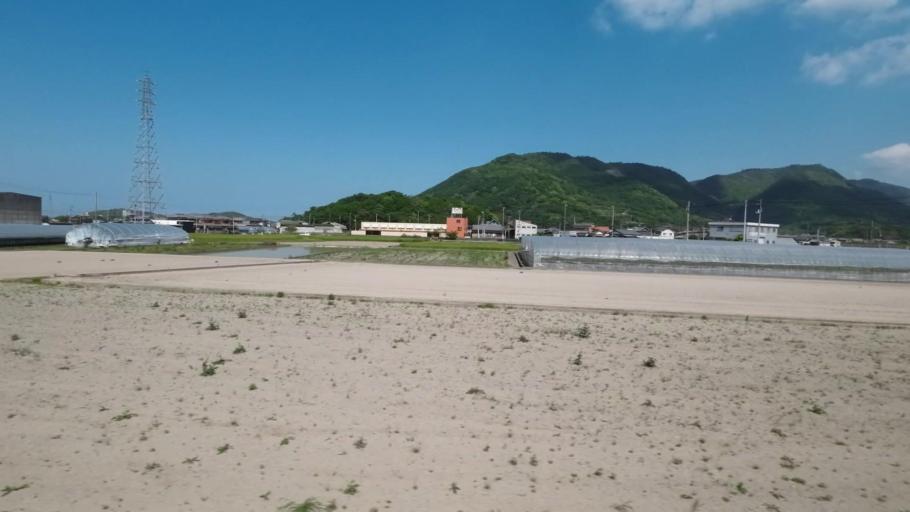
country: JP
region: Kagawa
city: Kan'onjicho
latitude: 34.1343
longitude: 133.6836
